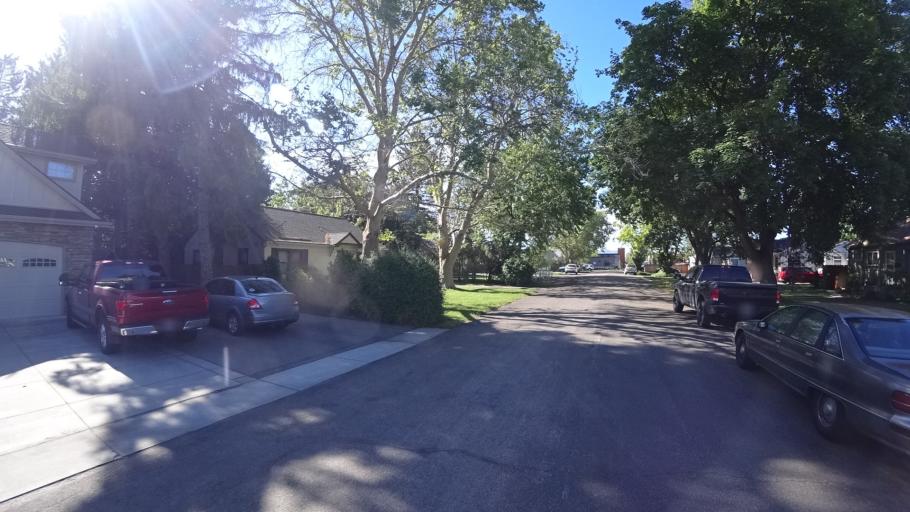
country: US
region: Idaho
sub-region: Ada County
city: Garden City
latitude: 43.6202
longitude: -116.2411
